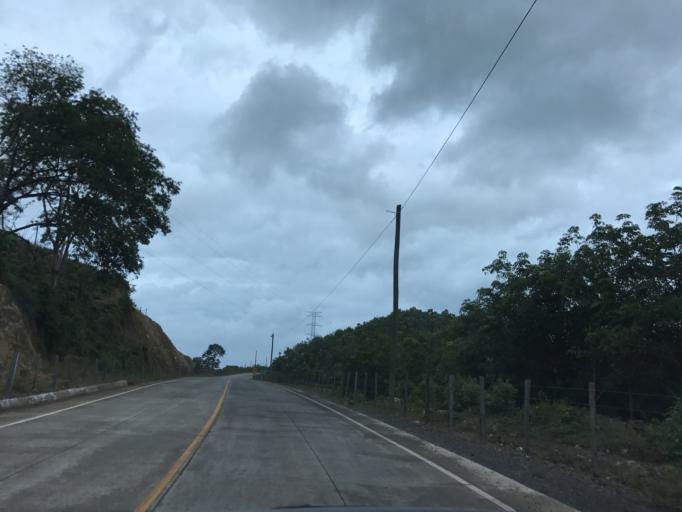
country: GT
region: Izabal
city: Morales
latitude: 15.6329
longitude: -89.0490
